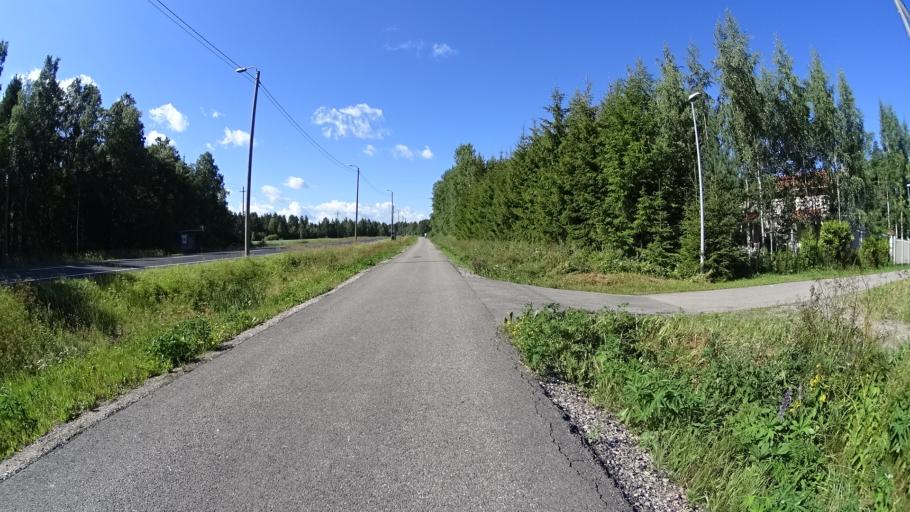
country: FI
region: Uusimaa
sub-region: Helsinki
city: Jaervenpaeae
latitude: 60.4351
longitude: 25.0638
